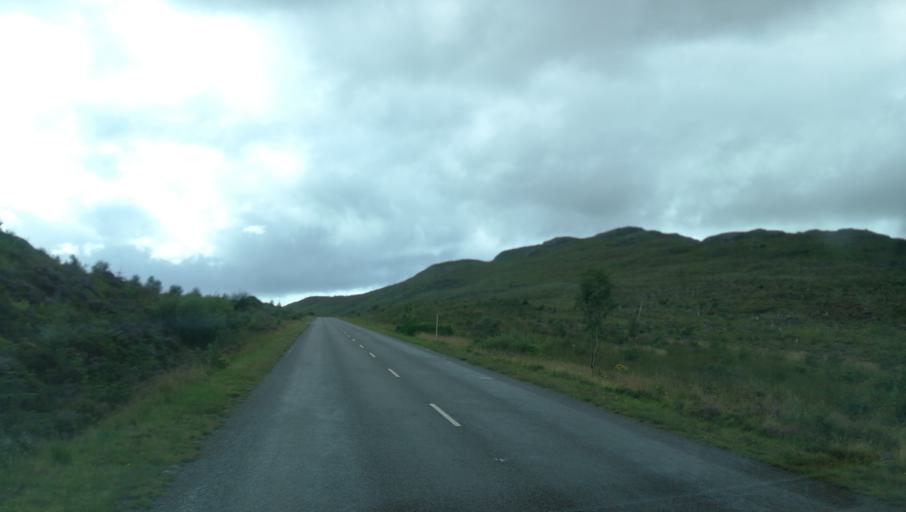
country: GB
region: Scotland
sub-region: Highland
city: Ullapool
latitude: 57.6918
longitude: -5.5731
